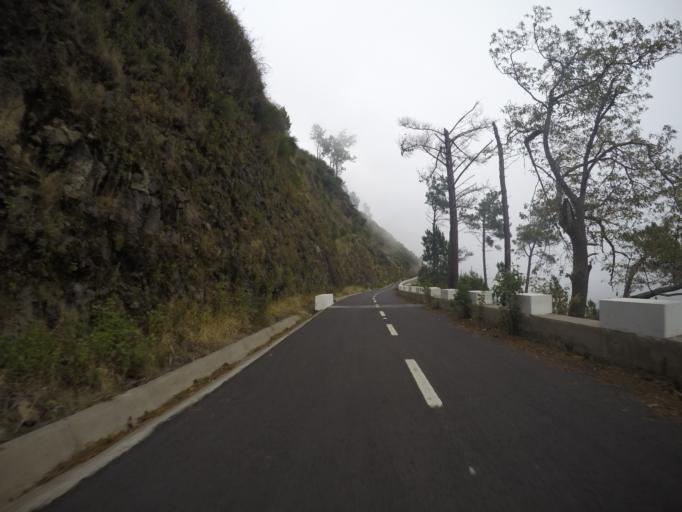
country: PT
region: Madeira
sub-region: Camara de Lobos
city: Curral das Freiras
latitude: 32.7049
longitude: -16.9563
